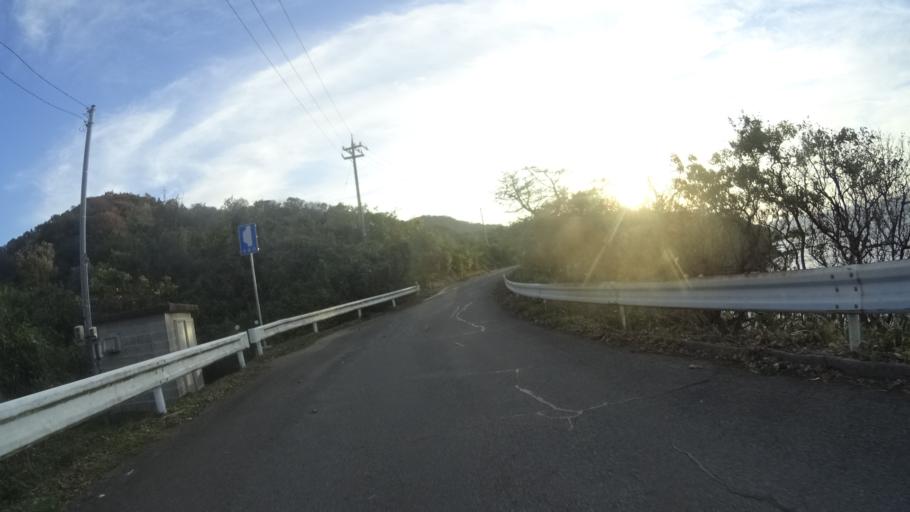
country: JP
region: Ishikawa
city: Nanao
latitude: 37.2160
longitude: 136.6957
